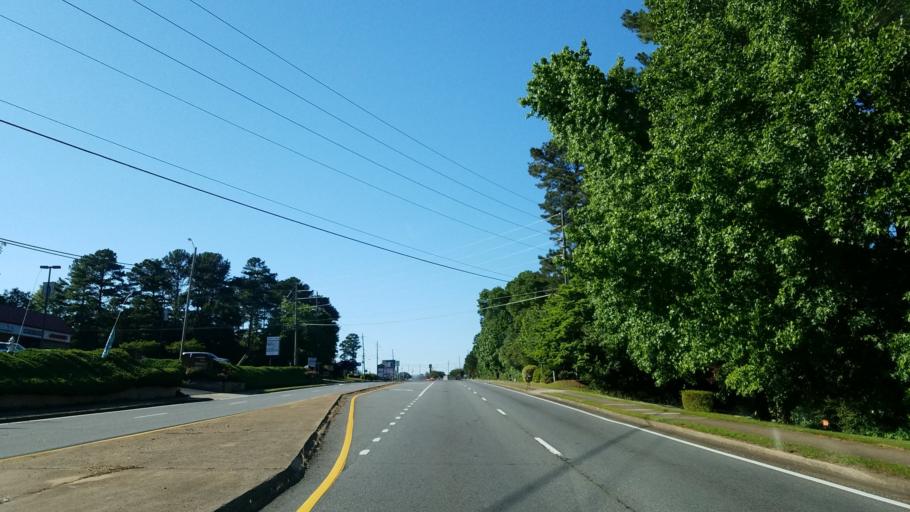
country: US
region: Georgia
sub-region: Cherokee County
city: Woodstock
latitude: 34.0813
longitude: -84.5746
